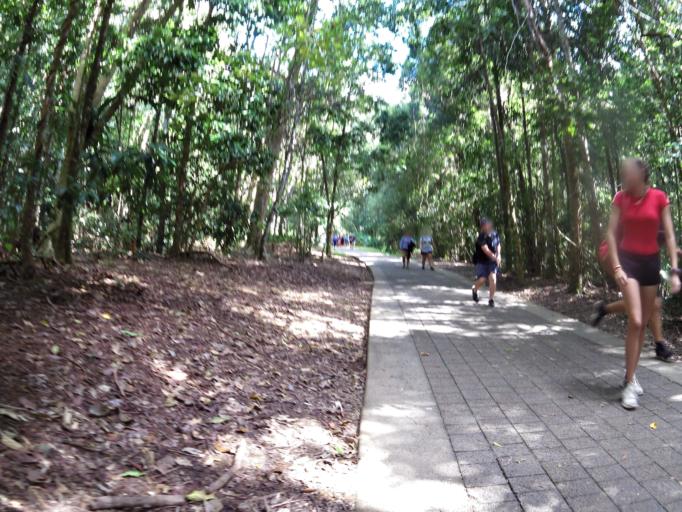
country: AU
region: Queensland
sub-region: Cairns
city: Woree
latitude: -16.9625
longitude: 145.6788
